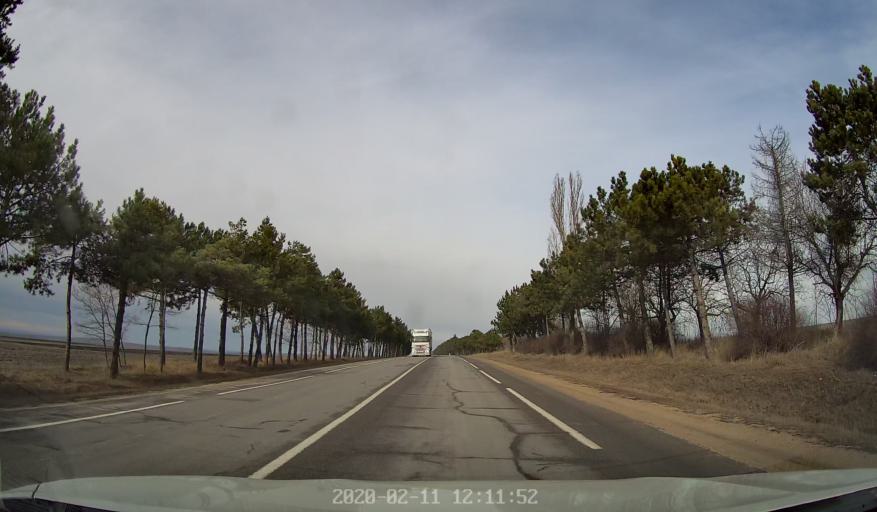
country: MD
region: Riscani
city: Riscani
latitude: 48.0572
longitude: 27.5111
